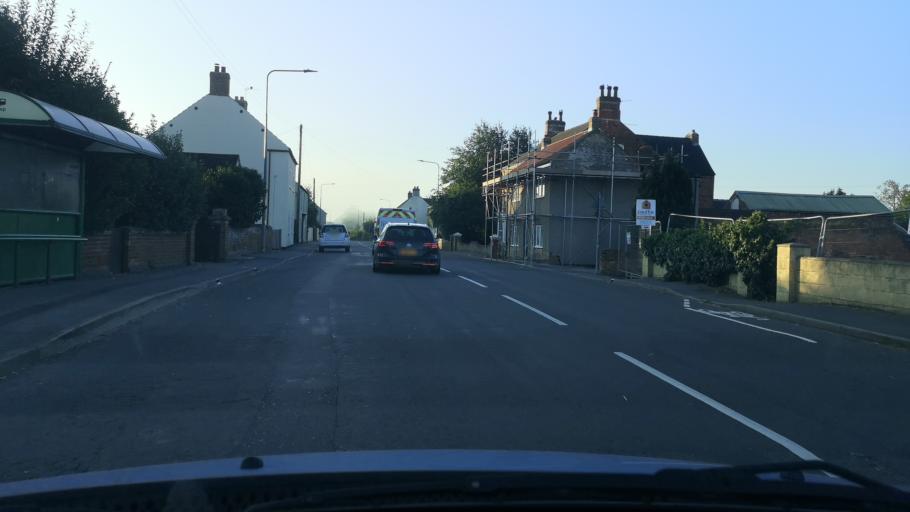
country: GB
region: England
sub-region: North Lincolnshire
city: Crowle
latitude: 53.6037
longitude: -0.8317
